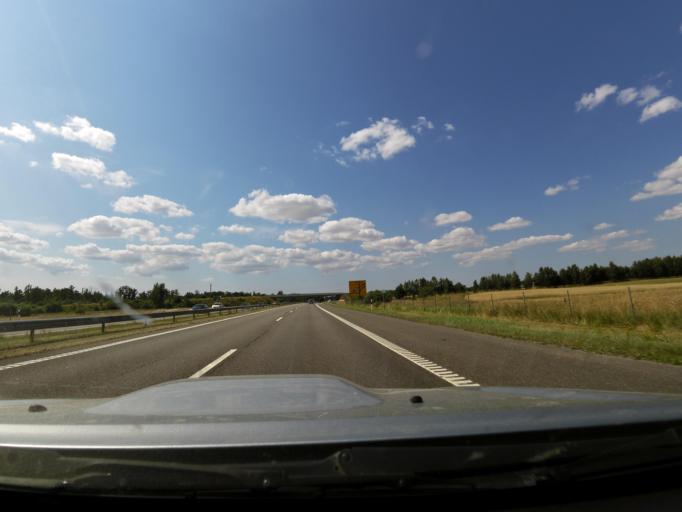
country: LT
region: Klaipedos apskritis
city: Gargzdai
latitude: 55.7095
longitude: 21.4854
